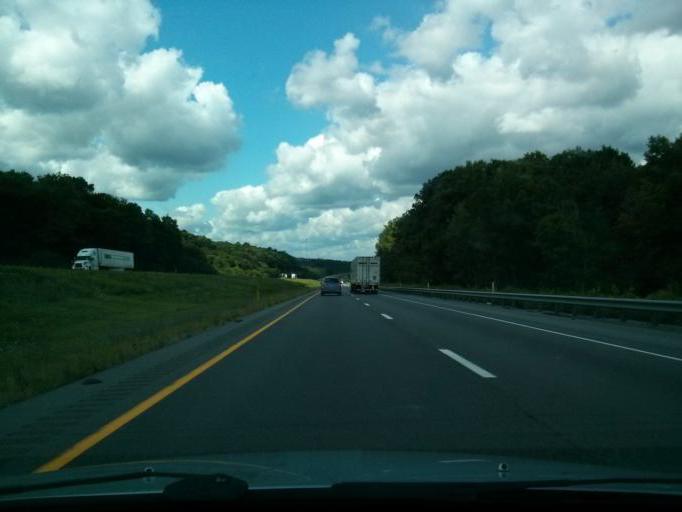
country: US
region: Pennsylvania
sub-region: Clearfield County
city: Treasure Lake
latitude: 41.1218
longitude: -78.6622
